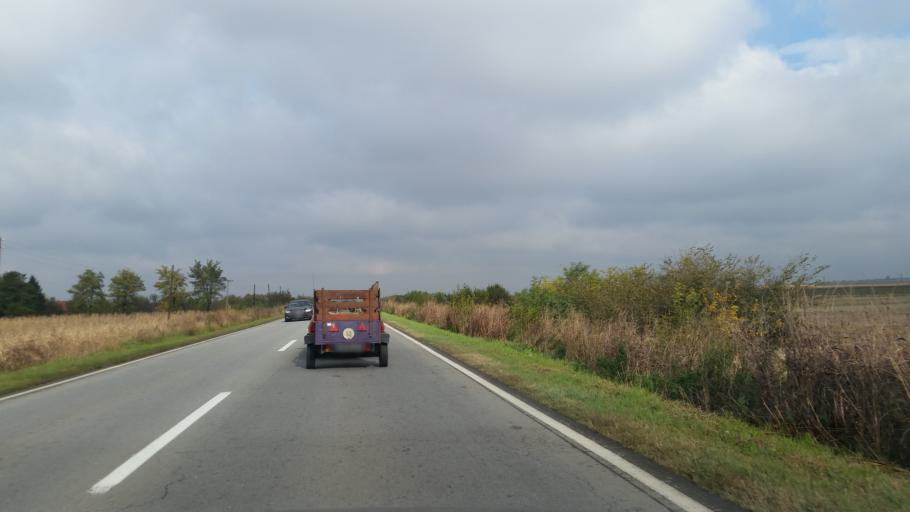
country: RS
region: Autonomna Pokrajina Vojvodina
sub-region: Srednjebanatski Okrug
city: Zrenjanin
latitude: 45.4228
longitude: 20.3710
